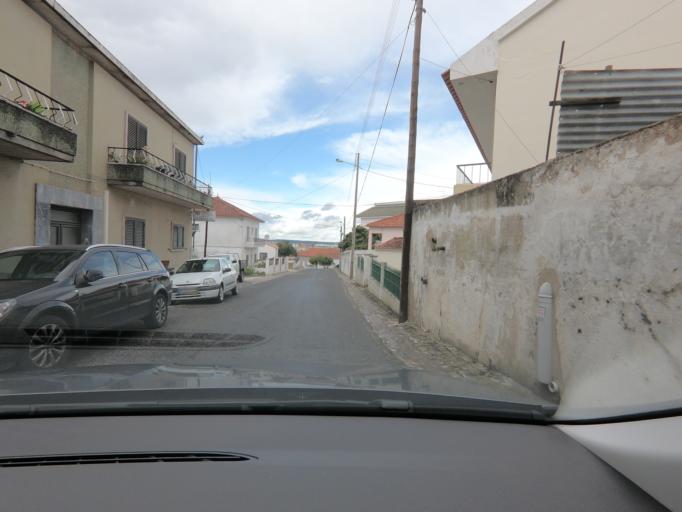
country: PT
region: Lisbon
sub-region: Alenquer
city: Carregado
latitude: 39.0200
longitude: -8.9924
